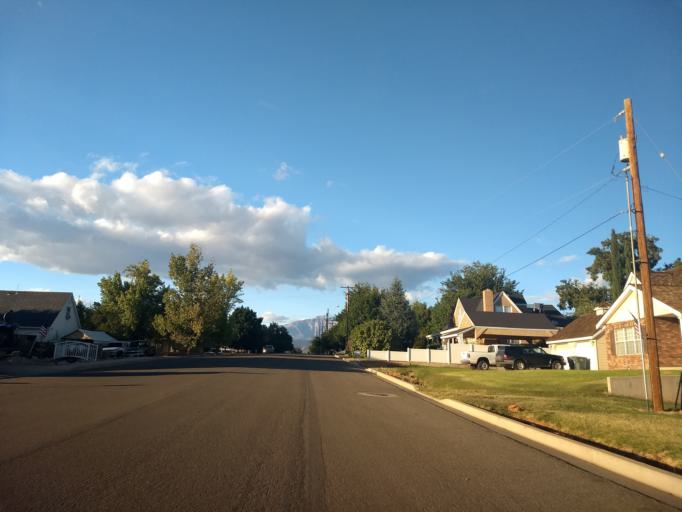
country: US
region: Utah
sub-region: Washington County
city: Washington
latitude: 37.1256
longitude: -113.5099
